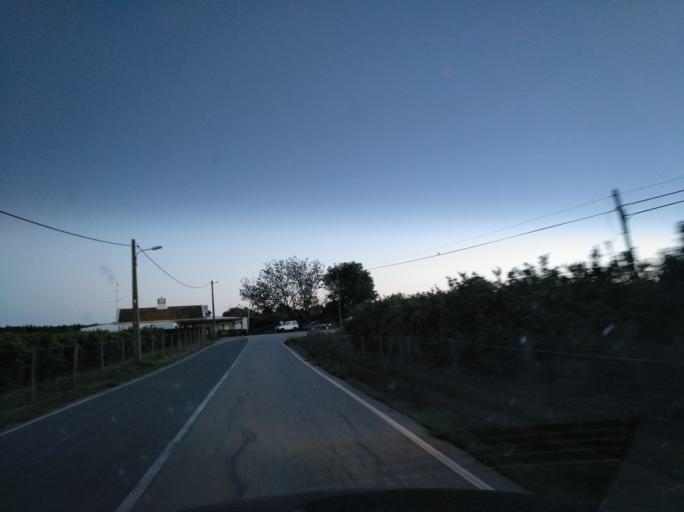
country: PT
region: Faro
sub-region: Vila Real de Santo Antonio
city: Monte Gordo
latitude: 37.1972
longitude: -7.5127
